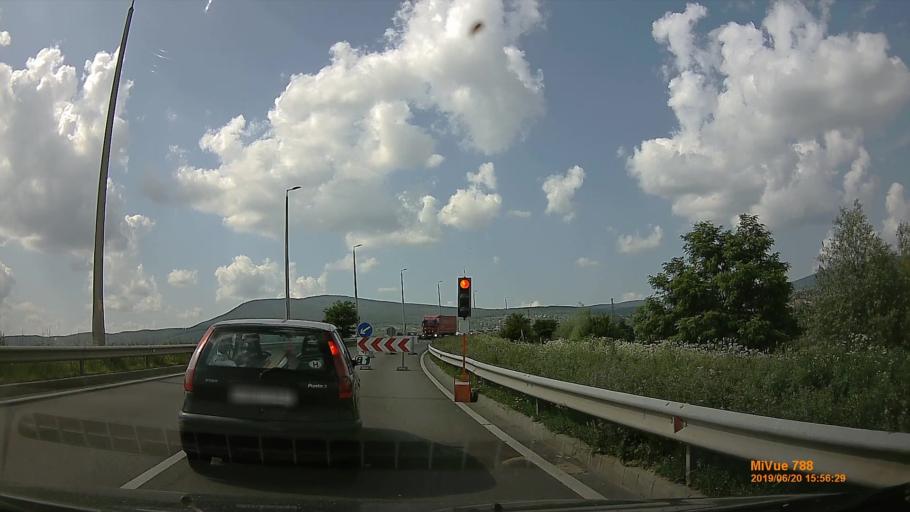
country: HU
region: Baranya
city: Pellerd
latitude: 46.0564
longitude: 18.1759
